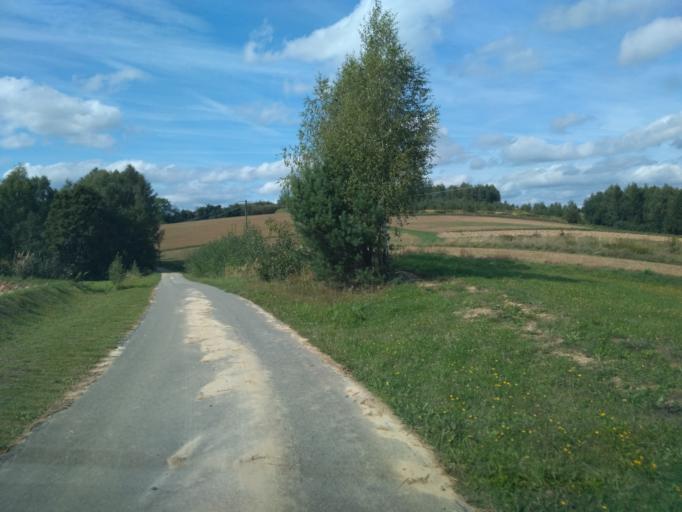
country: PL
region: Subcarpathian Voivodeship
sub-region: Powiat strzyzowski
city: Strzyzow
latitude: 49.8491
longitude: 21.8304
